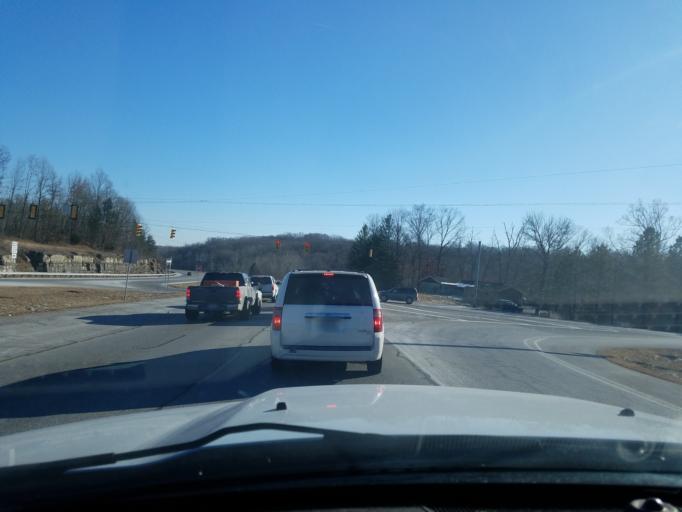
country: US
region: Indiana
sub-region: Lawrence County
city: Oolitic
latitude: 38.9102
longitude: -86.5455
